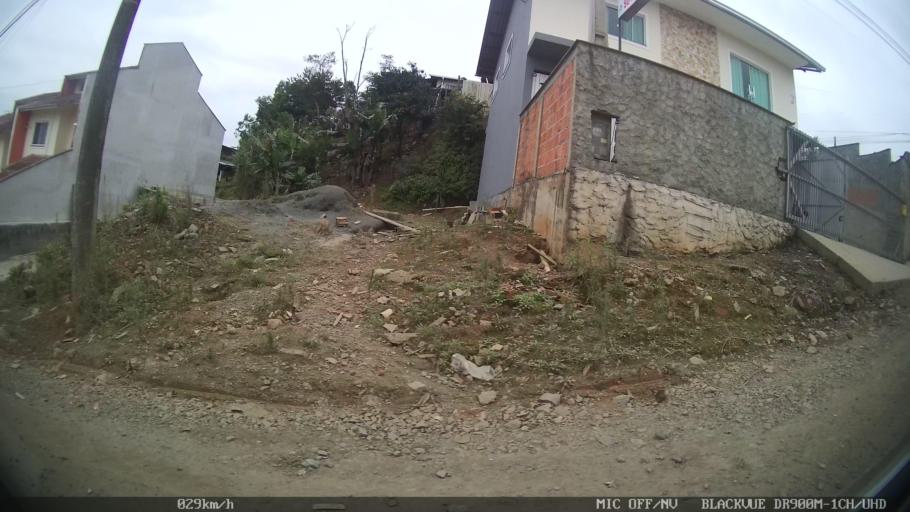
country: BR
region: Santa Catarina
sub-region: Joinville
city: Joinville
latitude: -26.3653
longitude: -48.8230
